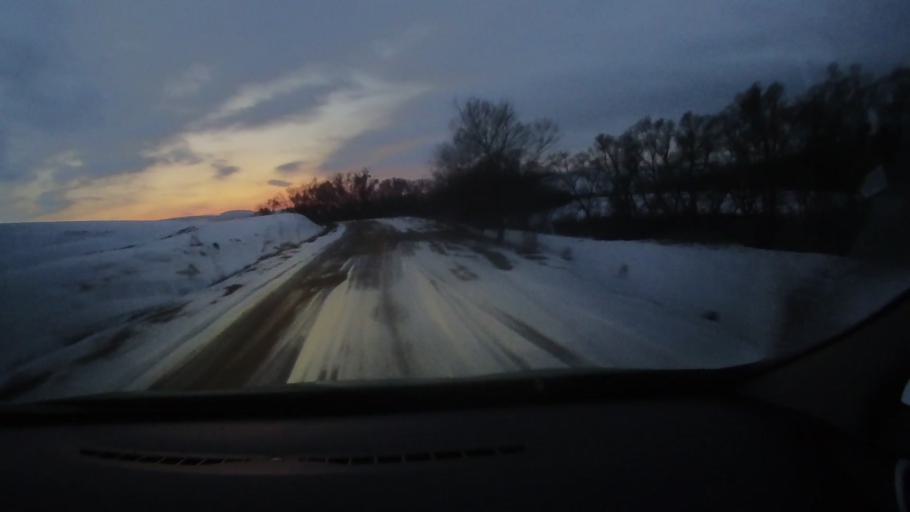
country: RO
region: Harghita
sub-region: Comuna Darjiu
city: Darjiu
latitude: 46.1654
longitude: 25.2181
